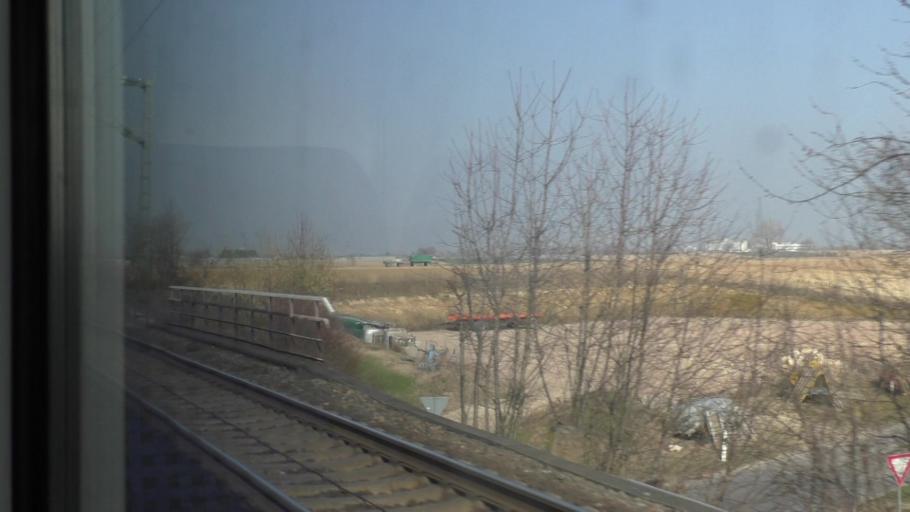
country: DE
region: Baden-Wuerttemberg
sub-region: Freiburg Region
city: Eschbach
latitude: 47.9025
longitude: 7.6735
